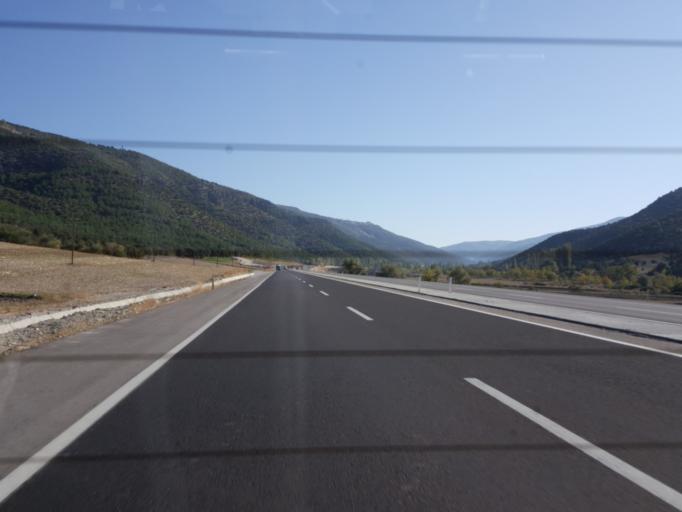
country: TR
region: Tokat
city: Turhal
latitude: 40.4669
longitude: 36.1219
